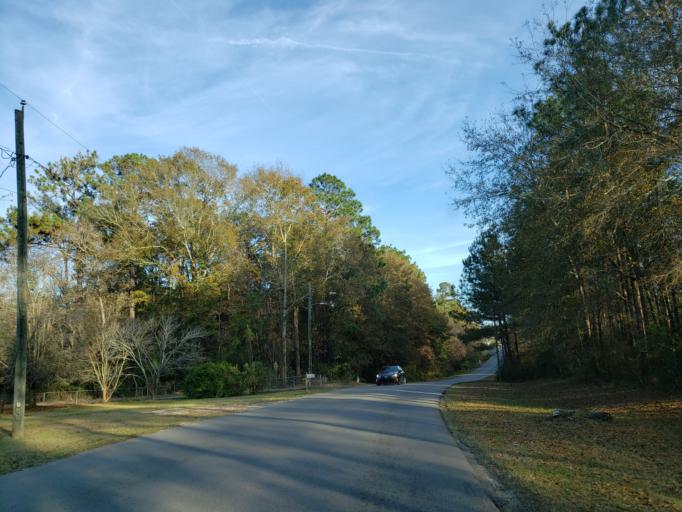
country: US
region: Mississippi
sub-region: Forrest County
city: Hattiesburg
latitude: 31.2992
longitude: -89.3211
